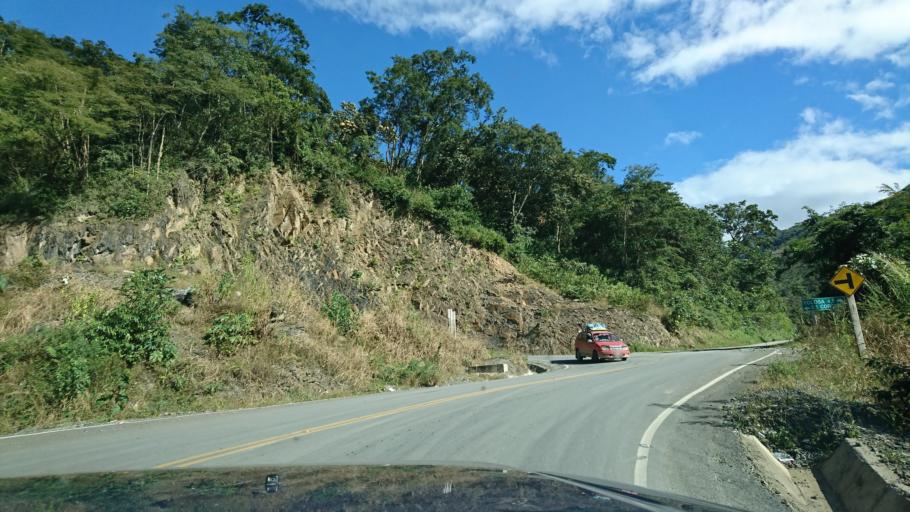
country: BO
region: La Paz
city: Coroico
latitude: -16.1979
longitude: -67.7416
